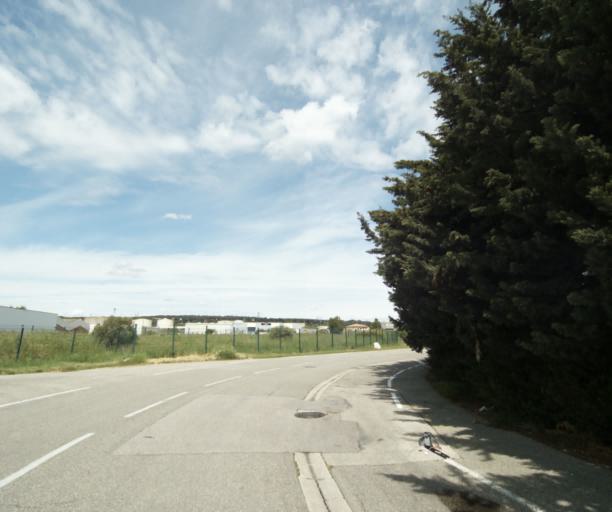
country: FR
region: Provence-Alpes-Cote d'Azur
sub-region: Departement des Bouches-du-Rhone
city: Rognac
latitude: 43.4986
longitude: 5.2219
